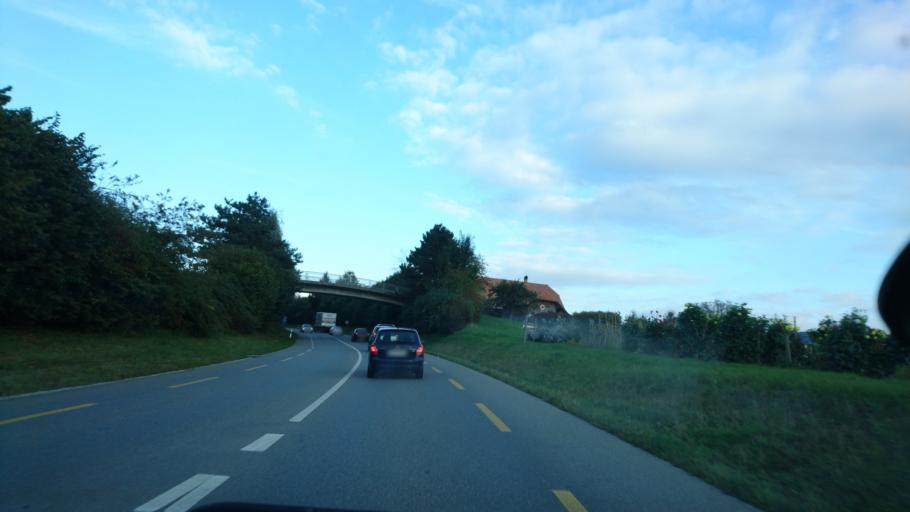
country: CH
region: Bern
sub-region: Bern-Mittelland District
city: Worb
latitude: 46.9175
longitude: 7.5861
